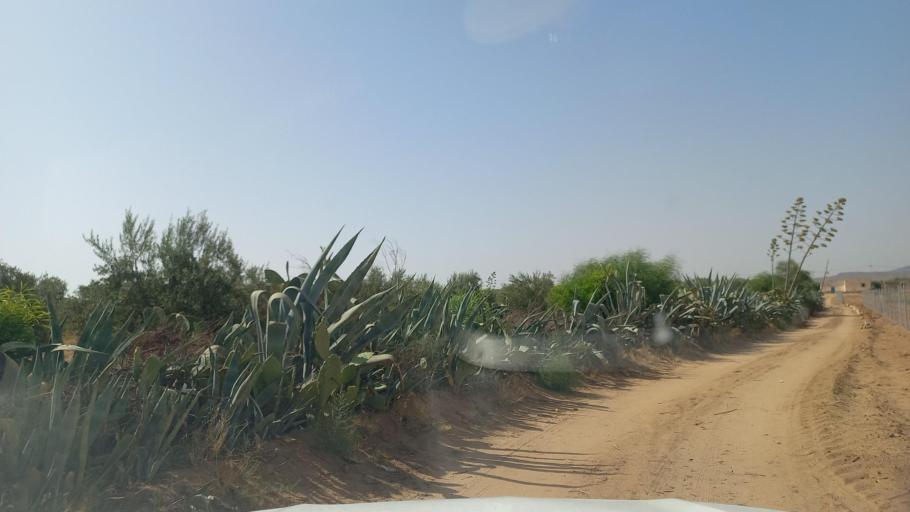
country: TN
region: Al Qasrayn
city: Kasserine
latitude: 35.2401
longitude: 9.0506
